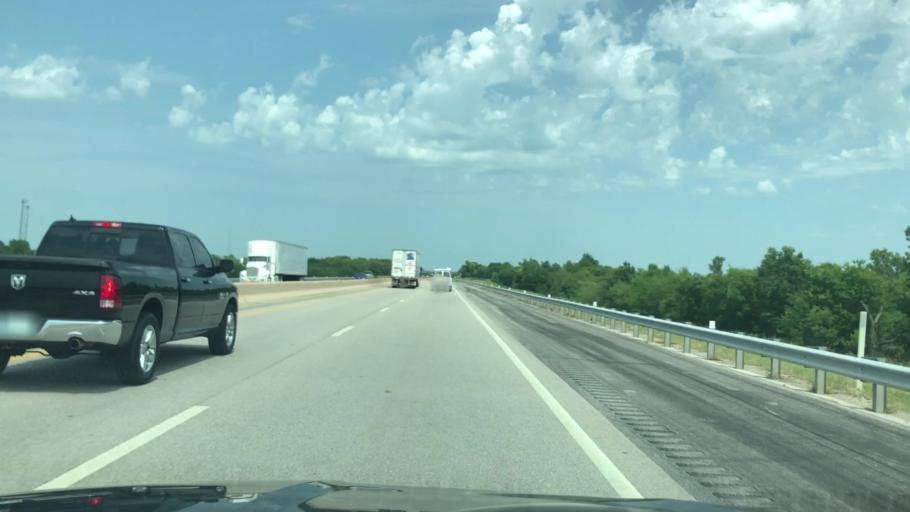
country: US
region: Oklahoma
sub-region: Rogers County
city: Verdigris
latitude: 36.2154
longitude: -95.6931
